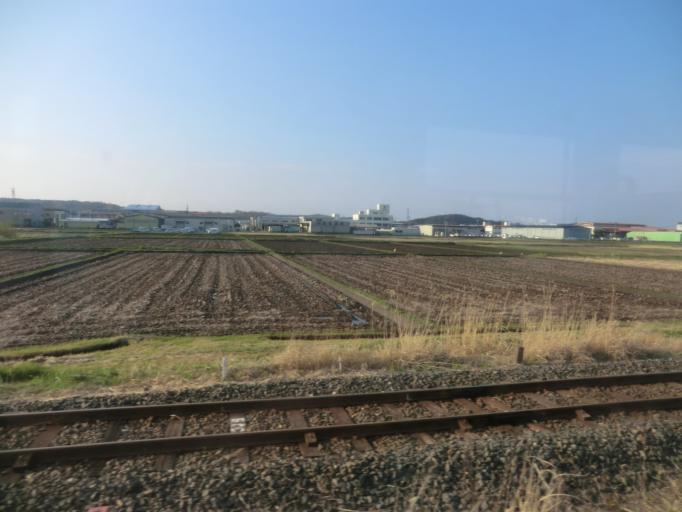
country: JP
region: Aomori
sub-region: Hachinohe Shi
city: Uchimaru
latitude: 40.5191
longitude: 141.4529
